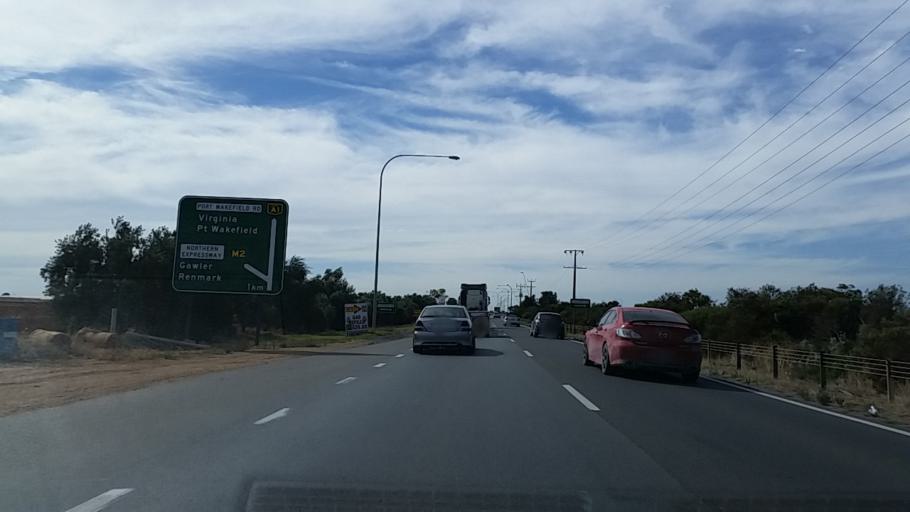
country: AU
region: South Australia
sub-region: Playford
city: Virginia
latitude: -34.7184
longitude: 138.5776
